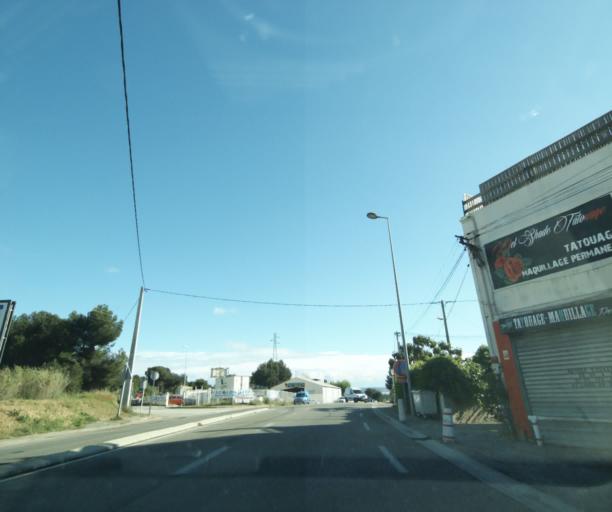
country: FR
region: Provence-Alpes-Cote d'Azur
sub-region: Departement des Bouches-du-Rhone
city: Vitrolles
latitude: 43.4581
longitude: 5.2330
